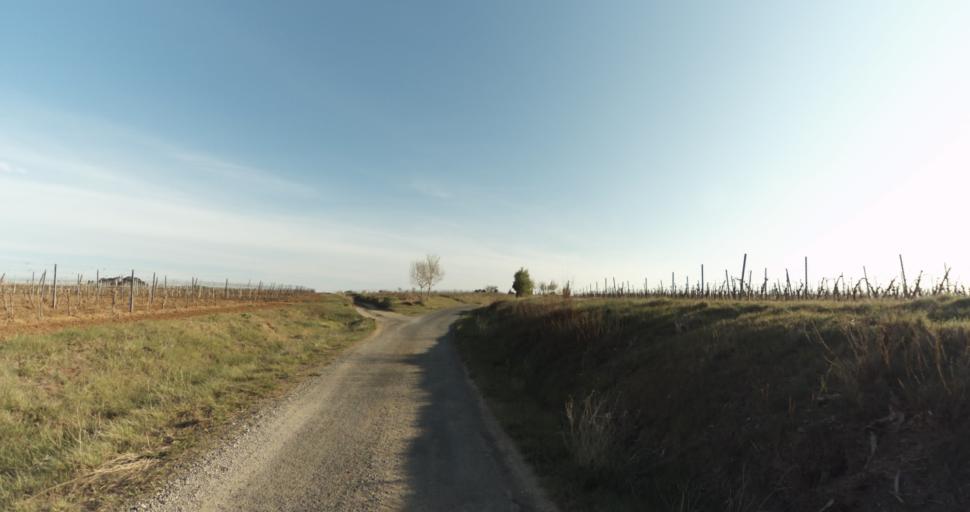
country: FR
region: Languedoc-Roussillon
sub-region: Departement de l'Herault
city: Marseillan
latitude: 43.3740
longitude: 3.5201
